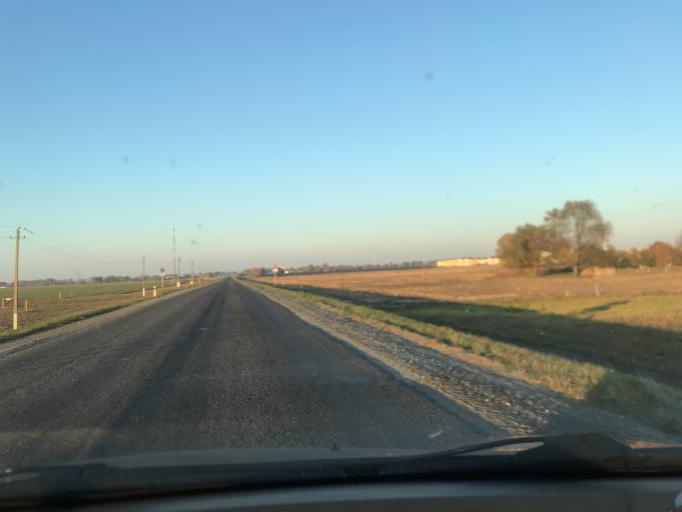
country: BY
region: Gomel
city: Brahin
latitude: 51.7780
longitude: 30.2505
